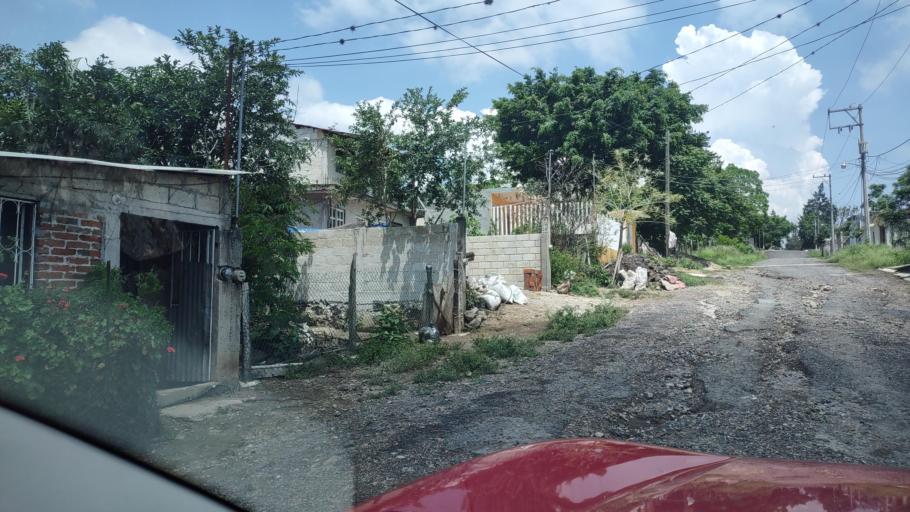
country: MX
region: Veracruz
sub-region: Emiliano Zapata
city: Dos Rios
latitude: 19.4895
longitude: -96.8123
